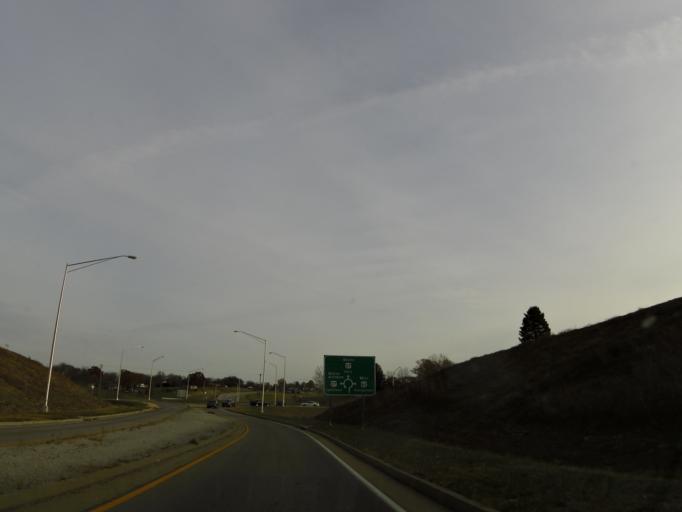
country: US
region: Kentucky
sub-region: Harrison County
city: Cynthiana
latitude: 38.3694
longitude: -84.3211
